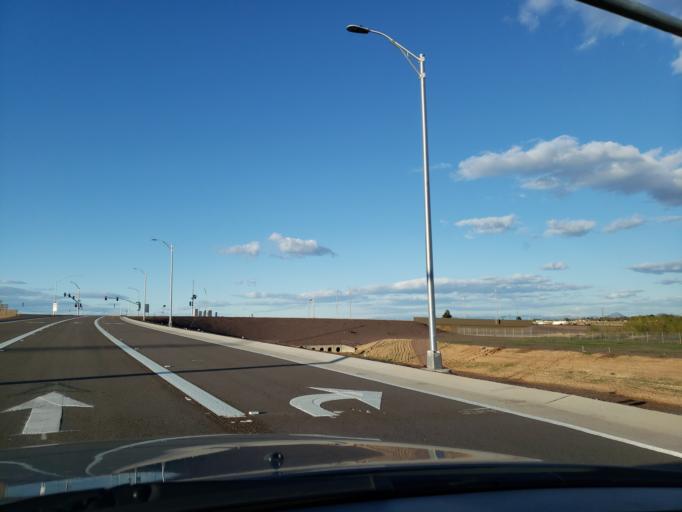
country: US
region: Arizona
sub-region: Maricopa County
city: Laveen
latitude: 33.3469
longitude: -112.1883
